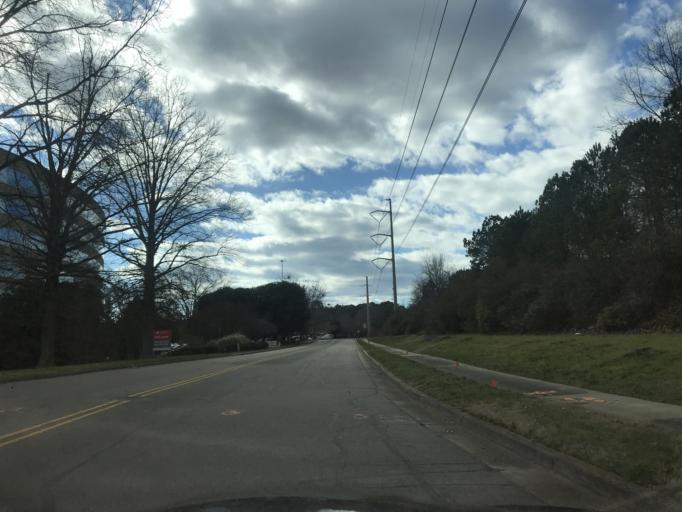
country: US
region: North Carolina
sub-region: Wake County
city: Cary
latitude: 35.7686
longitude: -78.7265
